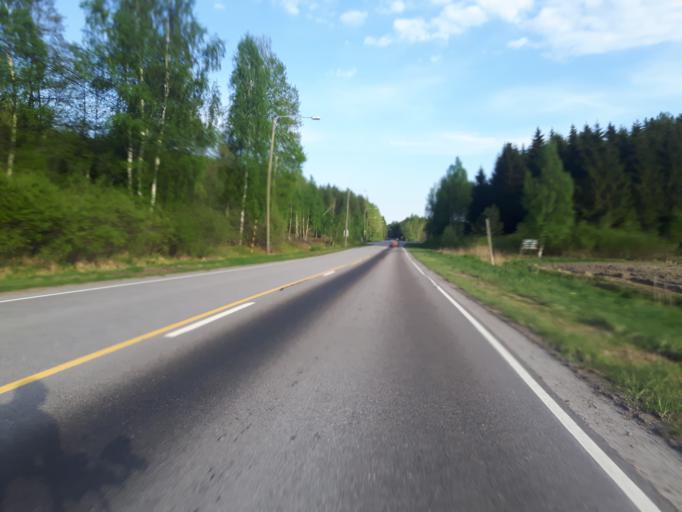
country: FI
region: Uusimaa
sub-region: Loviisa
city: Perna
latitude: 60.4654
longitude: 26.0337
